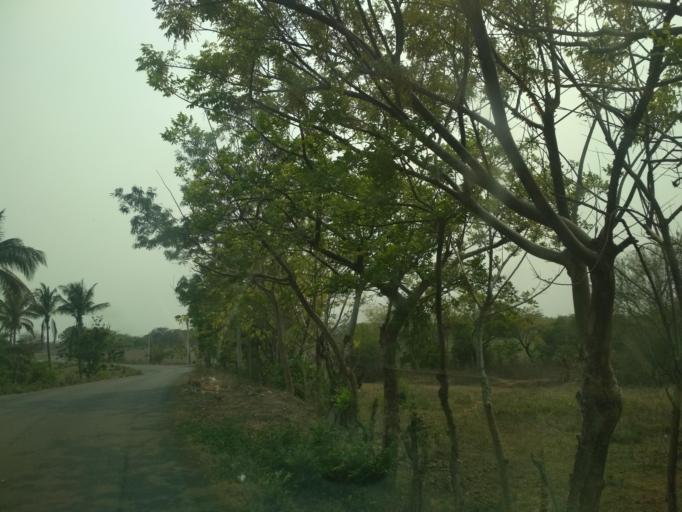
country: MX
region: Veracruz
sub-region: Veracruz
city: Delfino Victoria (Santa Fe)
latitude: 19.2100
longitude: -96.3186
